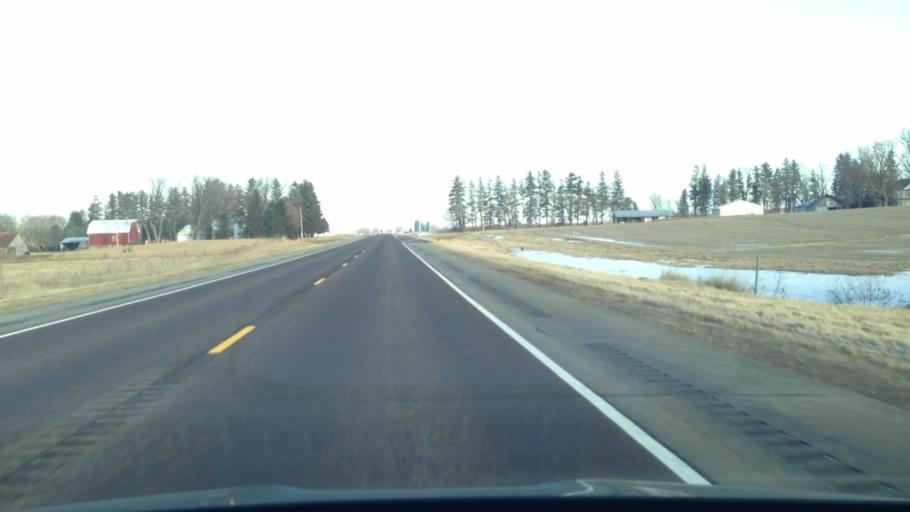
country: US
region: Minnesota
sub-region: Goodhue County
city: Goodhue
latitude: 44.3810
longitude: -92.6153
